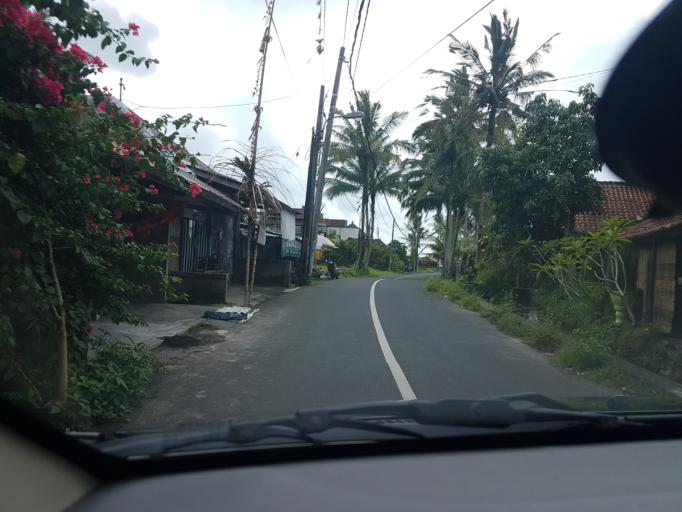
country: ID
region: Bali
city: Banjar Triwangsakeliki
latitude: -8.4598
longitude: 115.2745
